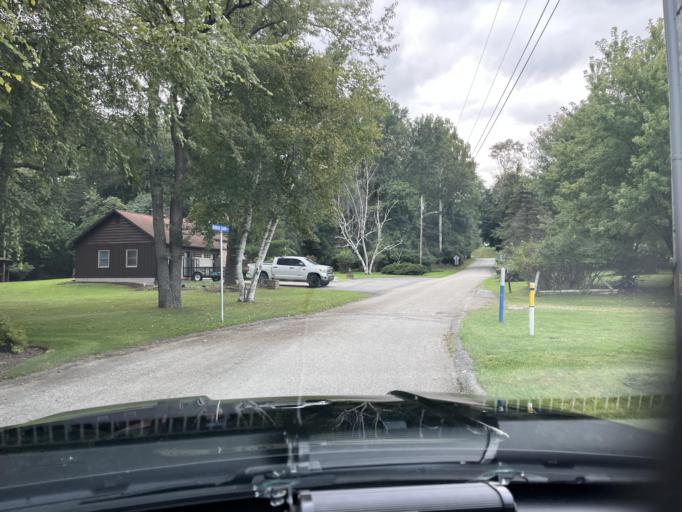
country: US
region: Pennsylvania
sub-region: Fayette County
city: Hopwood
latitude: 39.8735
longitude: -79.7027
